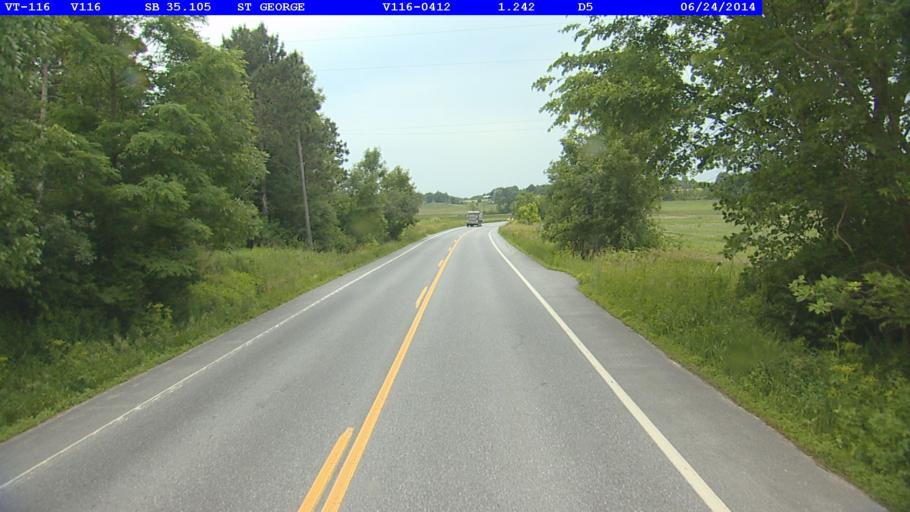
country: US
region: Vermont
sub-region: Chittenden County
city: Hinesburg
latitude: 44.3957
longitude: -73.1400
